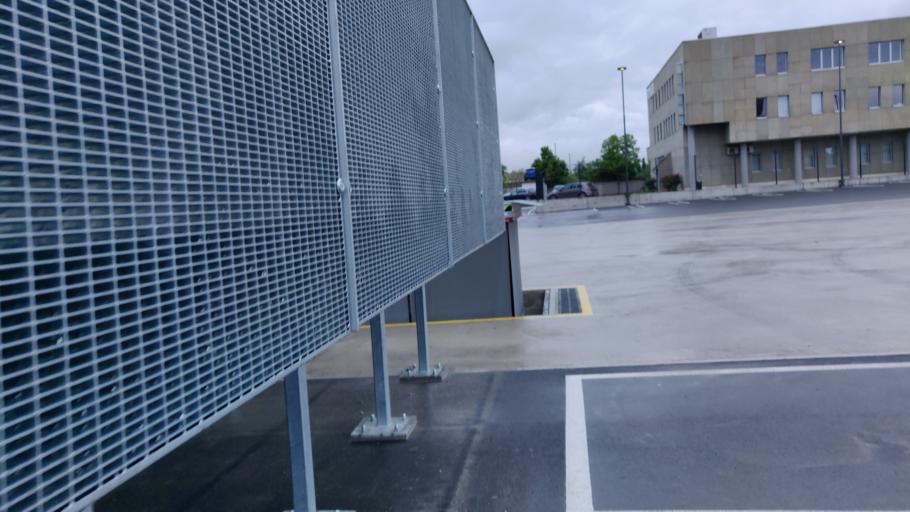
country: SI
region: Ljubljana
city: Ljubljana
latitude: 46.0789
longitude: 14.4848
